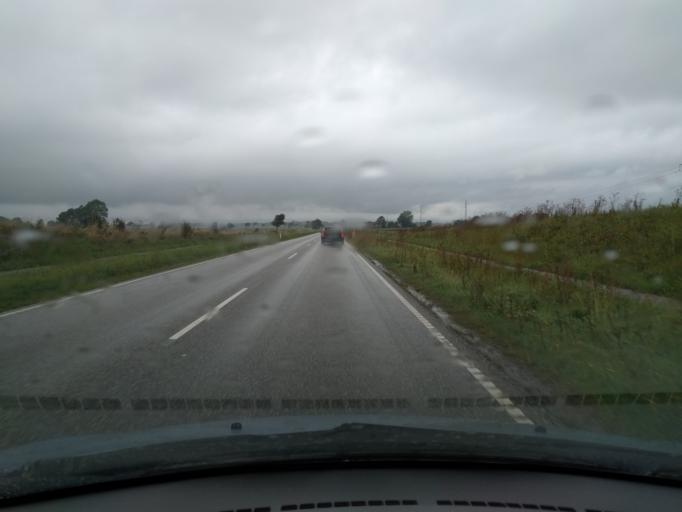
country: DK
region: Zealand
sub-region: Vordingborg Kommune
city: Neder Vindinge
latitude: 55.1234
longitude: 11.8191
